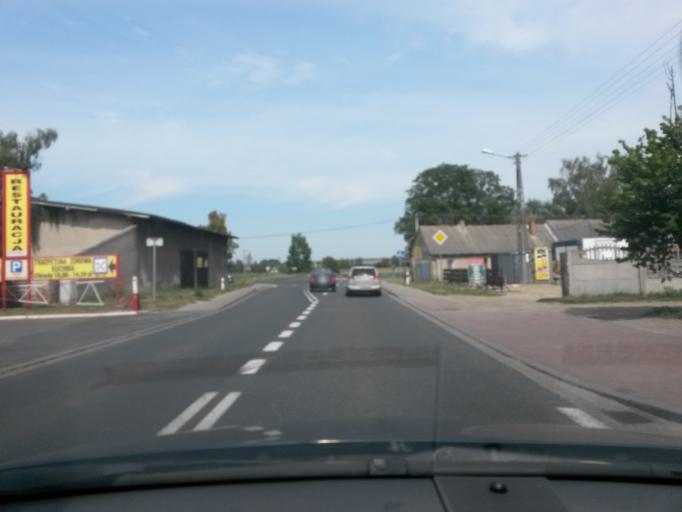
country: PL
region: Greater Poland Voivodeship
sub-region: Powiat gostynski
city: Gostyn
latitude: 51.9351
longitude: 17.0181
